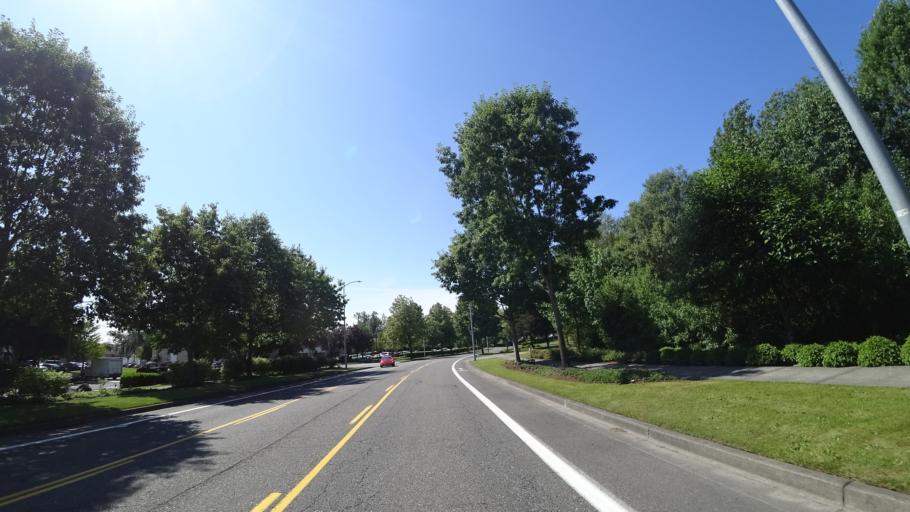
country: US
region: Oregon
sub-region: Multnomah County
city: Lents
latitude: 45.5716
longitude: -122.5727
